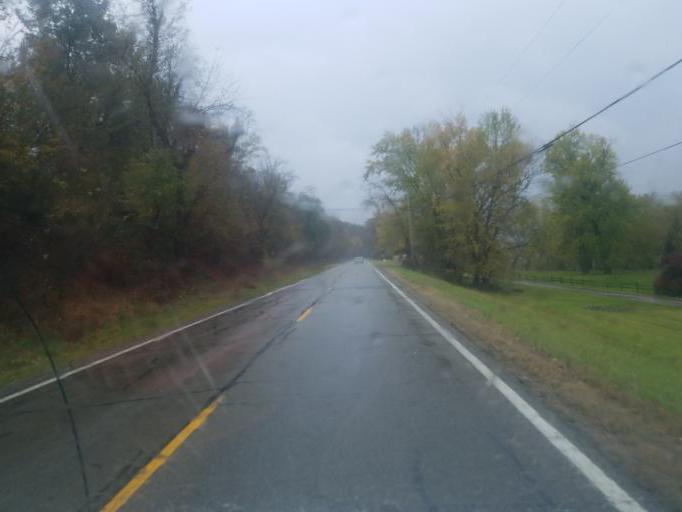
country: US
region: Ohio
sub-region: Muskingum County
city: South Zanesville
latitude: 39.8242
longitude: -81.8895
